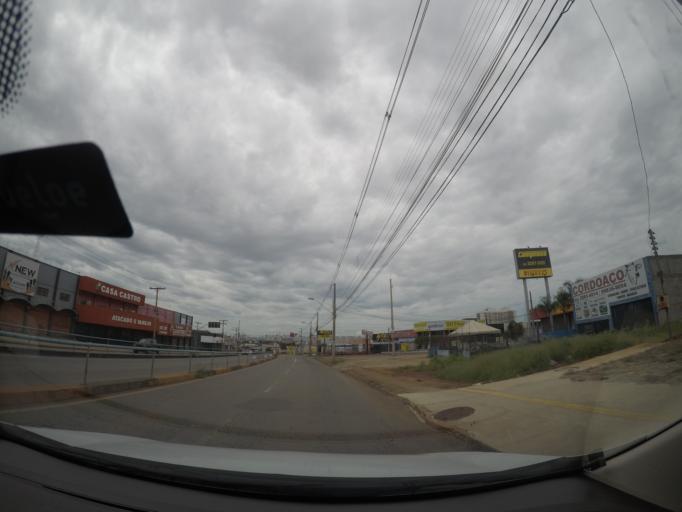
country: BR
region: Goias
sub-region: Goiania
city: Goiania
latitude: -16.6634
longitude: -49.3222
